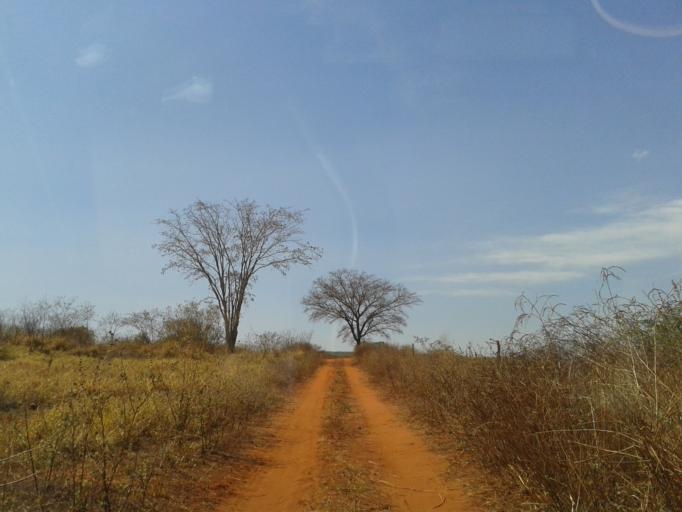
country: BR
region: Minas Gerais
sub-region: Santa Vitoria
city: Santa Vitoria
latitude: -19.2072
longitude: -50.0347
